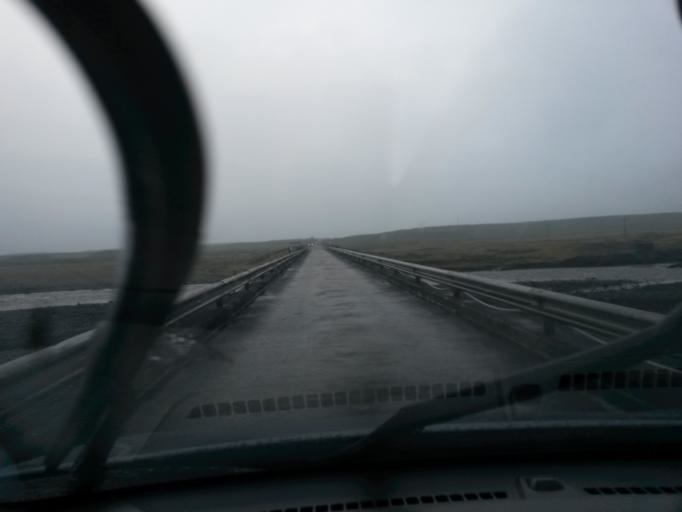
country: IS
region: South
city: Vestmannaeyjar
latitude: 63.4985
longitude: -19.4001
